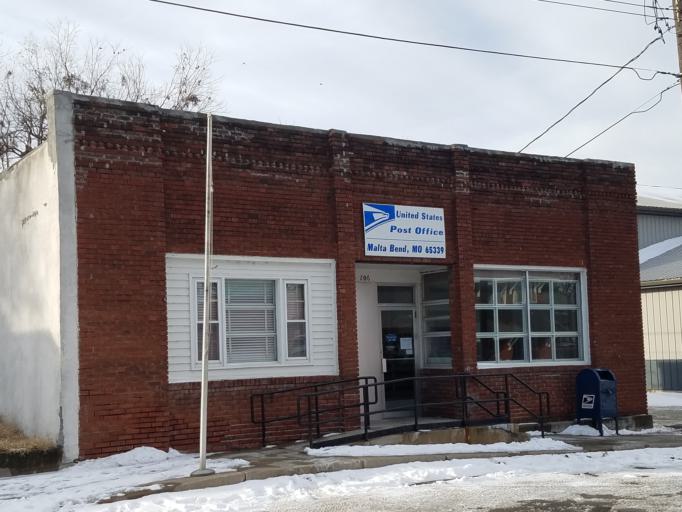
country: US
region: Missouri
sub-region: Saline County
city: Marshall
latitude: 39.1941
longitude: -93.3622
